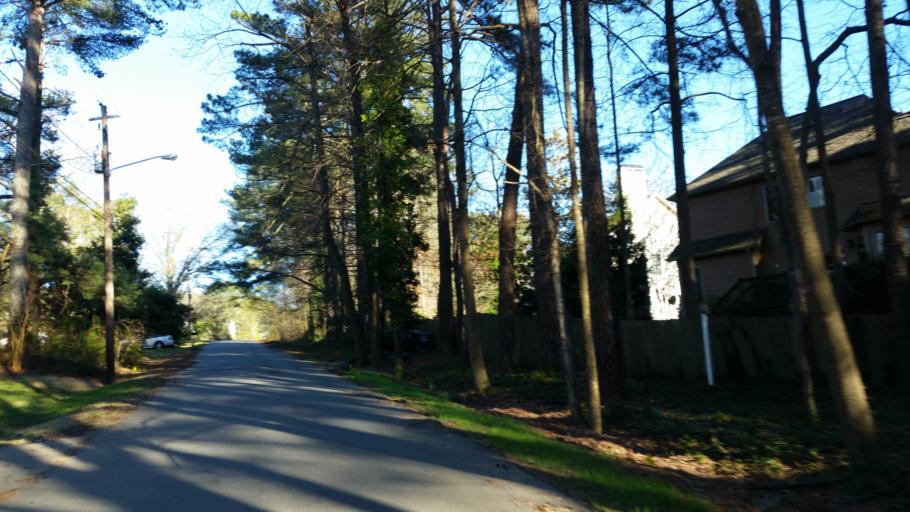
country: US
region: Georgia
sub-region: Cherokee County
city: Woodstock
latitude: 34.0284
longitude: -84.5358
